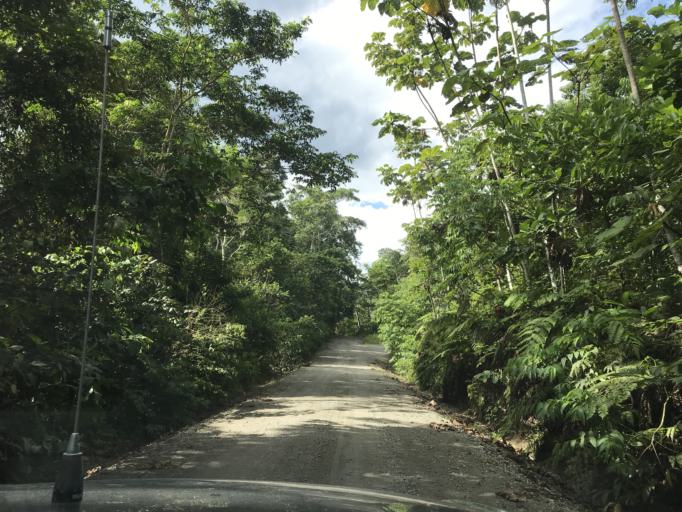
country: EC
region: Orellana
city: Puerto Francisco de Orellana
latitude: -0.6784
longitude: -76.3987
